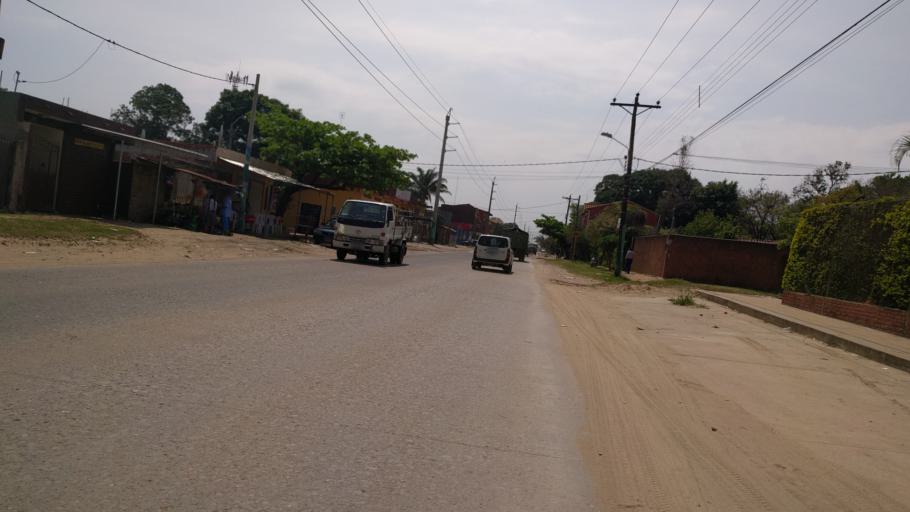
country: BO
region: Santa Cruz
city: Santa Cruz de la Sierra
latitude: -17.8489
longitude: -63.2175
